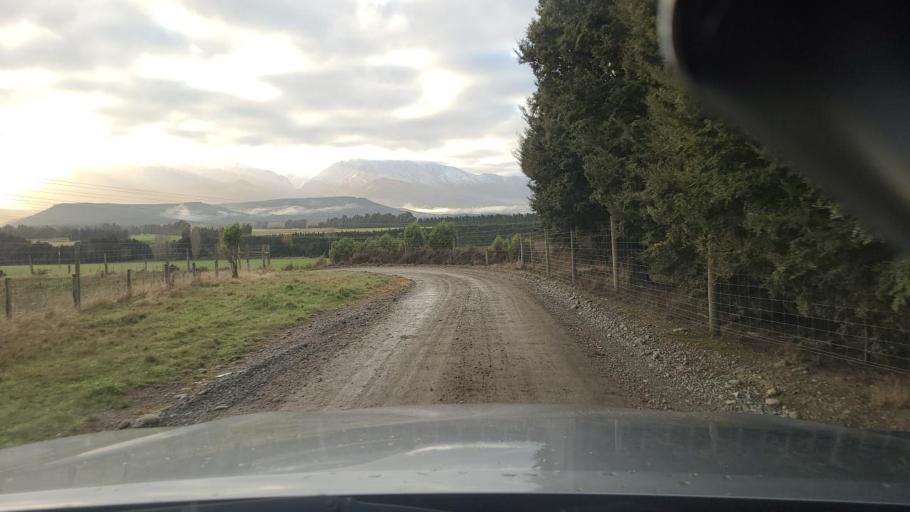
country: NZ
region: Southland
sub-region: Southland District
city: Te Anau
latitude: -45.8062
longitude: 167.6368
